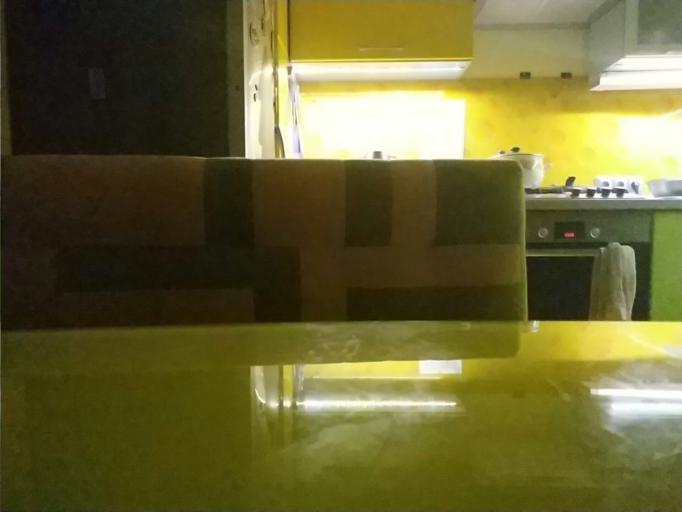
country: RU
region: Republic of Karelia
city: Pyaozerskiy
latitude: 65.8476
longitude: 30.4512
